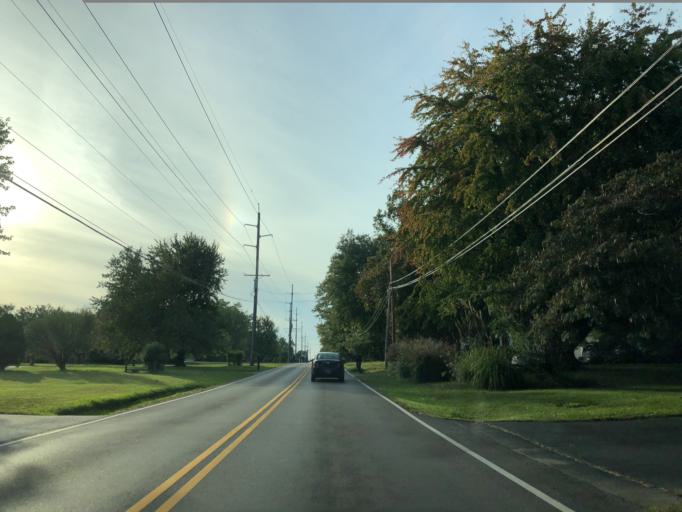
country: US
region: Ohio
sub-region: Warren County
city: Loveland Park
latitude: 39.2895
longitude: -84.2789
